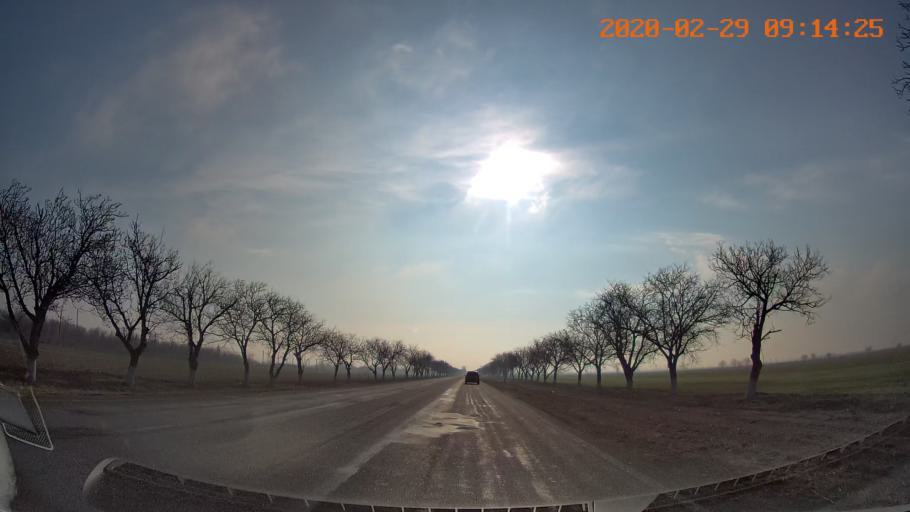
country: MD
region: Telenesti
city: Pervomaisc
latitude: 46.8088
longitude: 29.8526
